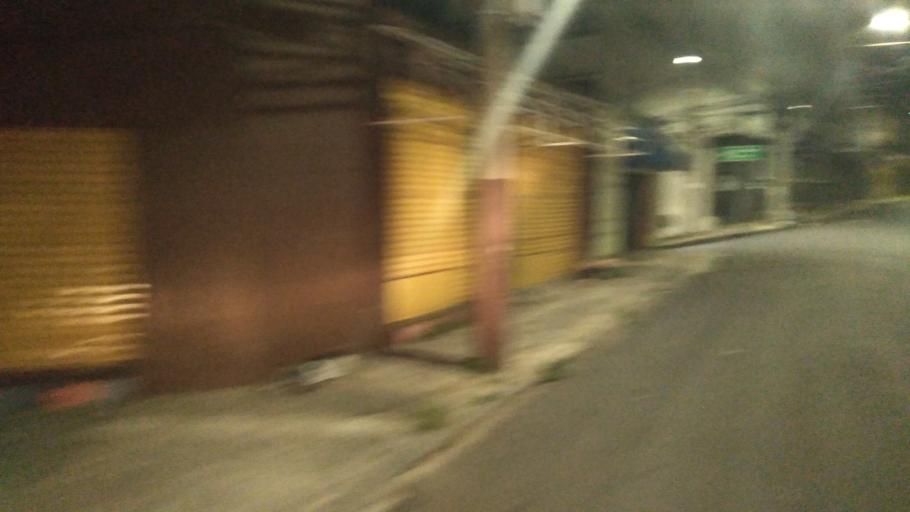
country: BR
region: Minas Gerais
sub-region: Belo Horizonte
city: Belo Horizonte
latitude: -19.9120
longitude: -43.9474
